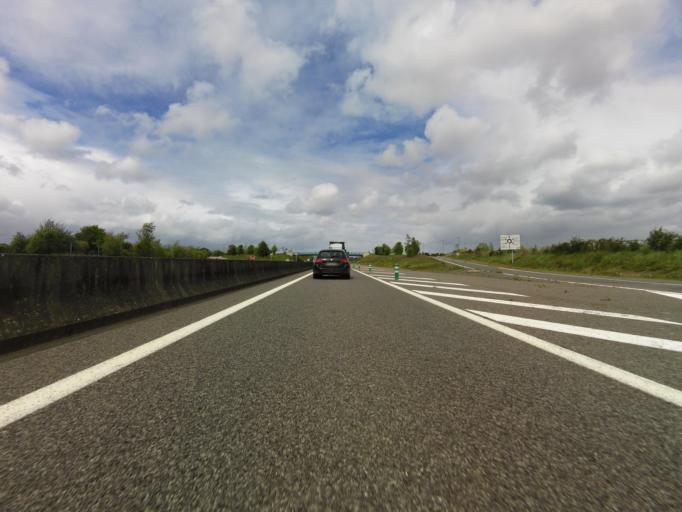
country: FR
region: Brittany
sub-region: Departement du Morbihan
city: Allaire
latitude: 47.6305
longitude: -2.1730
